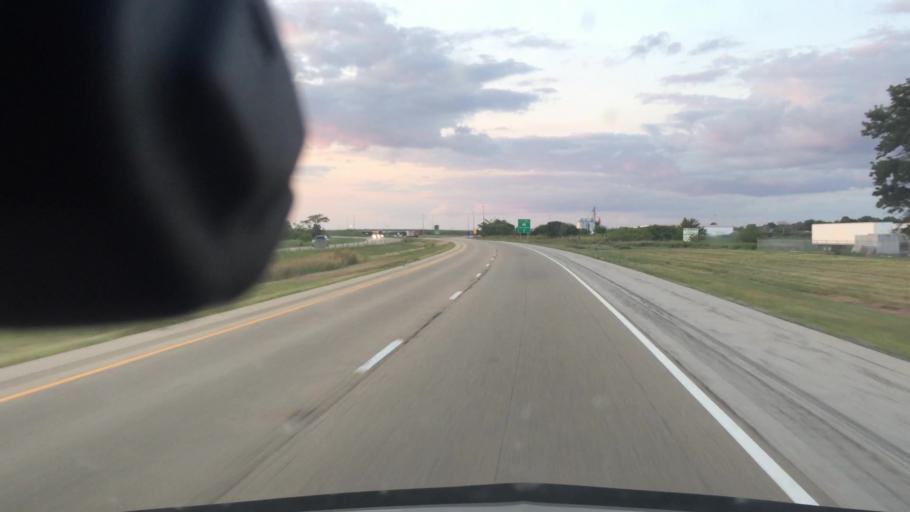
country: US
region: Illinois
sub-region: Grundy County
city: Gardner
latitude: 41.1778
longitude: -88.3239
